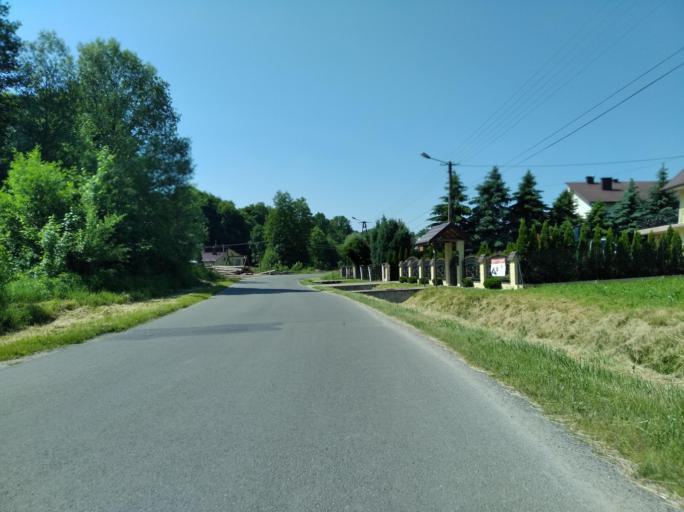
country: PL
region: Subcarpathian Voivodeship
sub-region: Powiat ropczycko-sedziszowski
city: Zagorzyce
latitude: 50.0128
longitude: 21.6711
